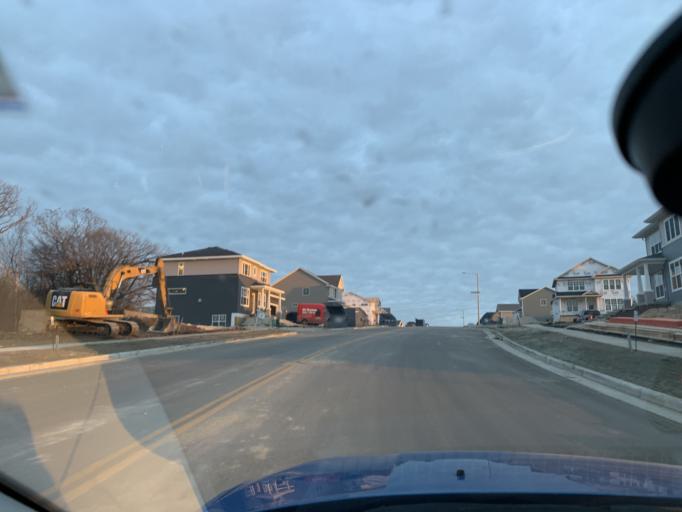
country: US
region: Wisconsin
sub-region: Dane County
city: Verona
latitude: 43.0479
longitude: -89.5598
